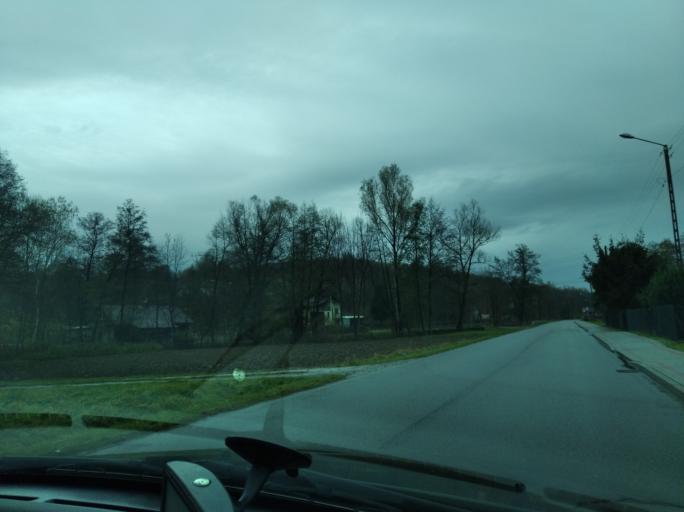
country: PL
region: Subcarpathian Voivodeship
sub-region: Powiat rzeszowski
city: Straszydle
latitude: 49.9128
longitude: 21.9604
